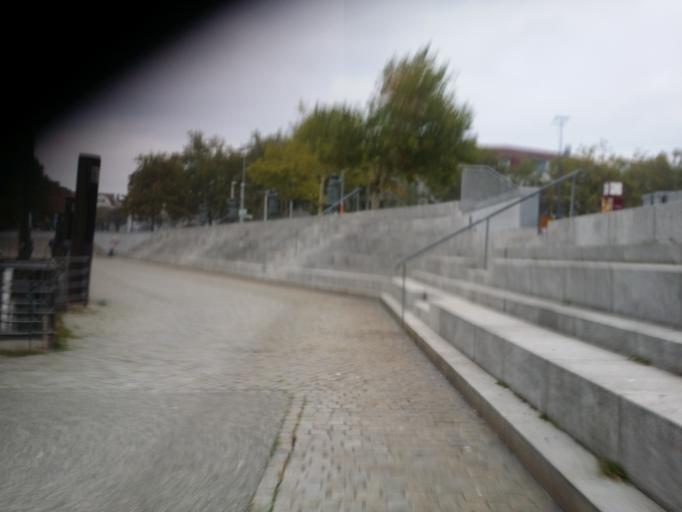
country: DE
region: Lower Saxony
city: Lemwerder
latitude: 53.1692
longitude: 8.6275
